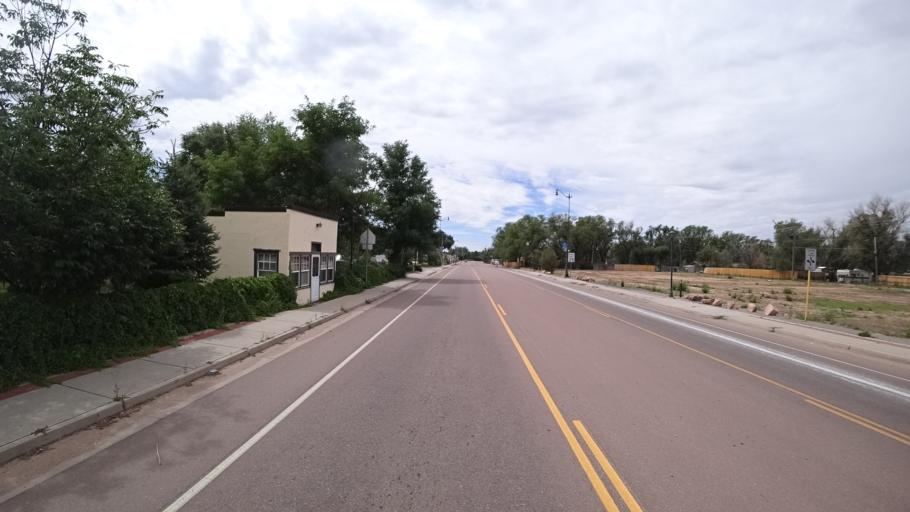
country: US
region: Colorado
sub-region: El Paso County
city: Fountain
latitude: 38.6821
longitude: -104.7045
